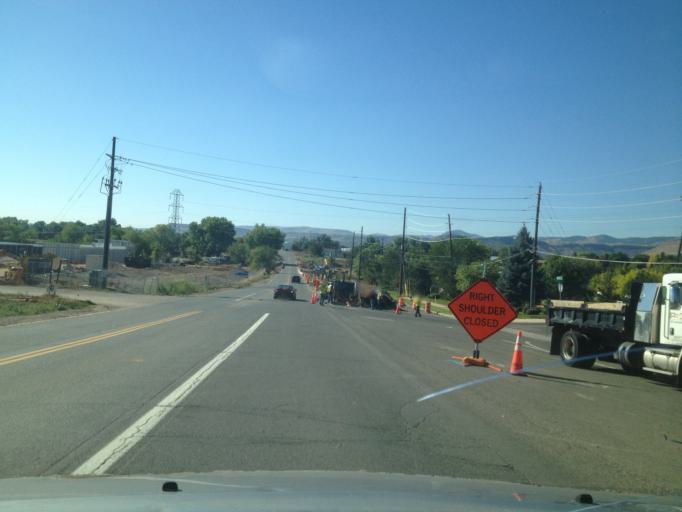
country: US
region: Colorado
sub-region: Jefferson County
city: Applewood
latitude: 39.8027
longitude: -105.1747
